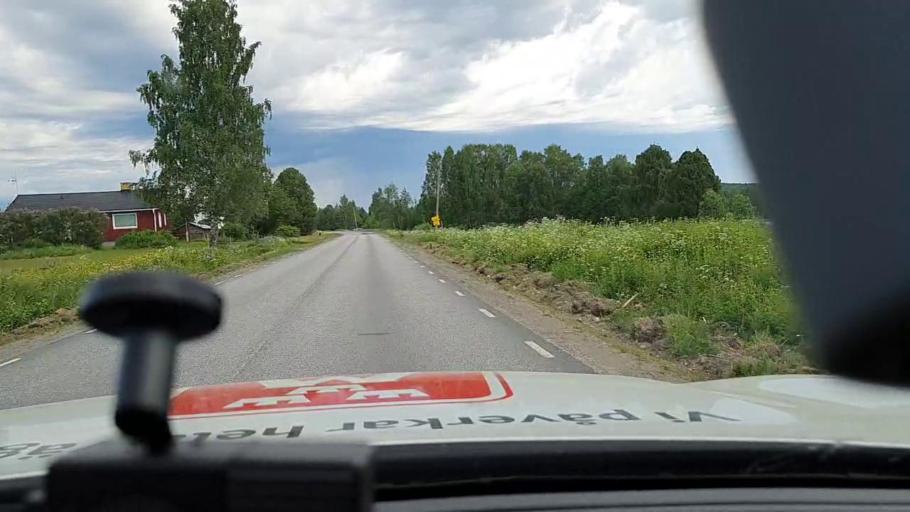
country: SE
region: Norrbotten
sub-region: Bodens Kommun
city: Saevast
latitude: 65.7661
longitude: 21.6909
